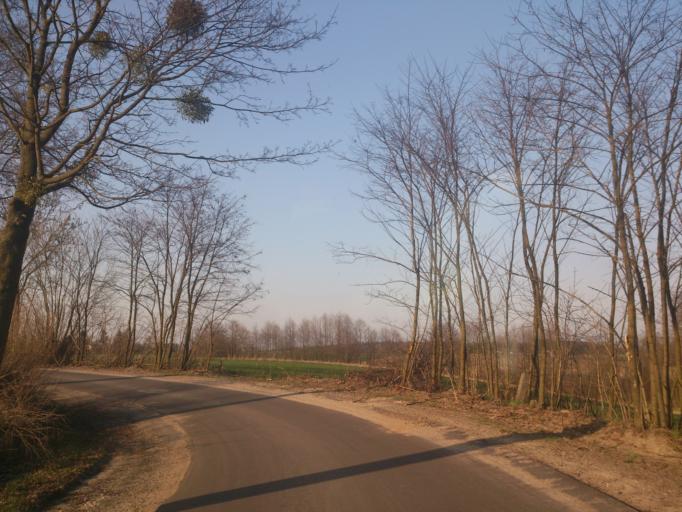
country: PL
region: Kujawsko-Pomorskie
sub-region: Powiat golubsko-dobrzynski
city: Radomin
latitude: 53.1187
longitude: 19.1389
